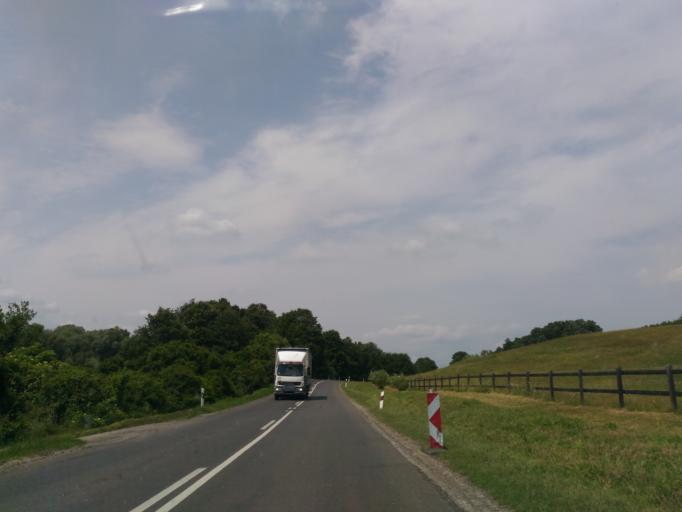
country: HU
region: Baranya
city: Komlo
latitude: 46.1704
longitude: 18.2134
